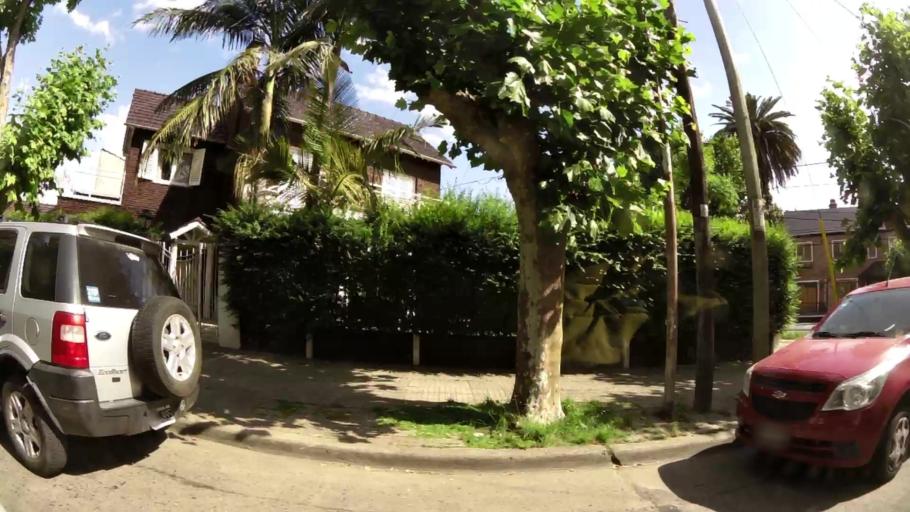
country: AR
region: Buenos Aires
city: San Justo
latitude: -34.6410
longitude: -58.5567
